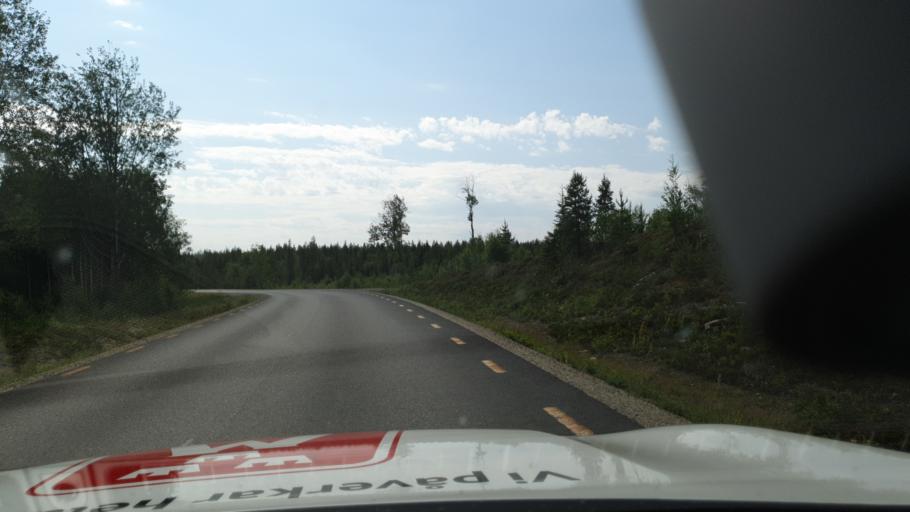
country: SE
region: Vaesterbotten
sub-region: Vindelns Kommun
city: Vindeln
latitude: 64.4237
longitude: 19.3534
